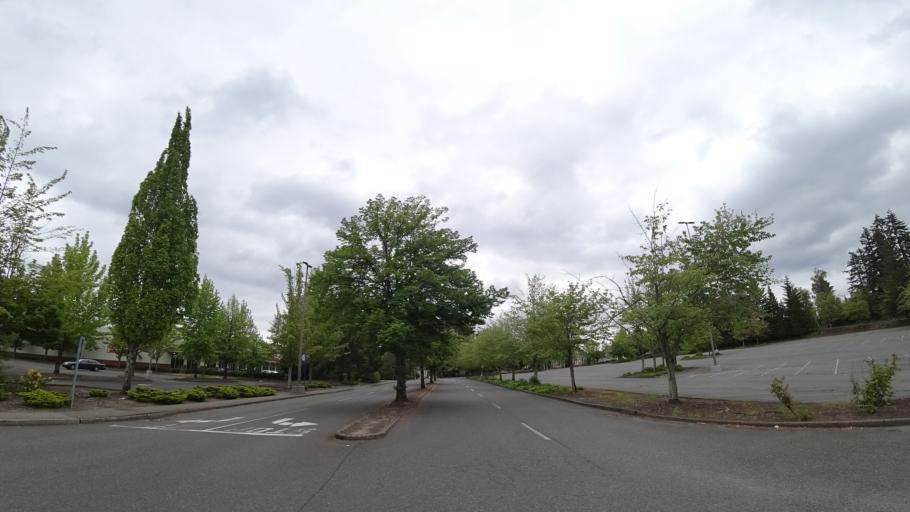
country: US
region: Oregon
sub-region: Washington County
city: Metzger
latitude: 45.4514
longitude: -122.7763
